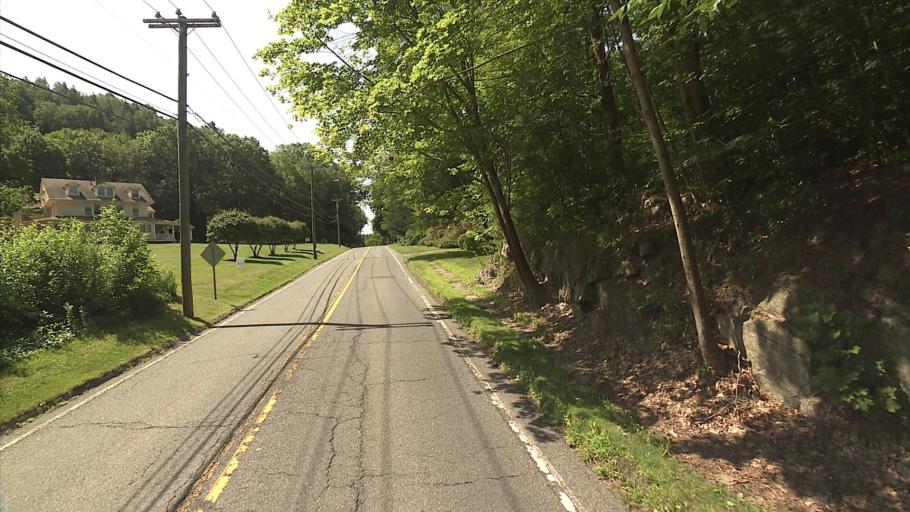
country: US
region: Connecticut
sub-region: Litchfield County
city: Winchester Center
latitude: 41.9854
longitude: -73.2003
